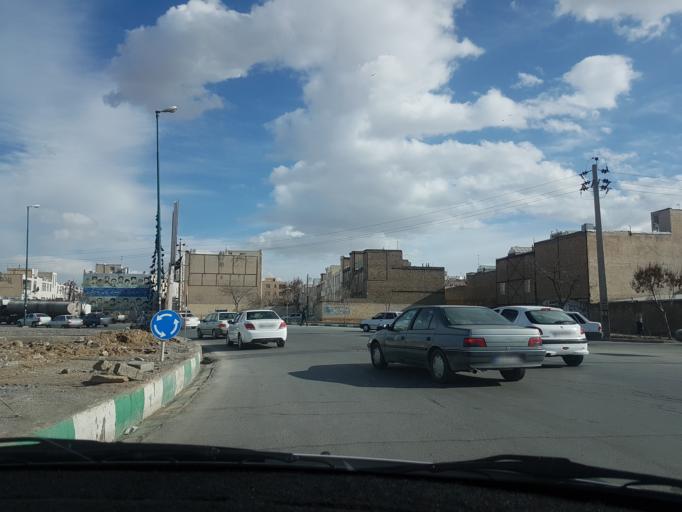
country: IR
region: Markazi
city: Arak
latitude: 34.1189
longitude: 49.7047
